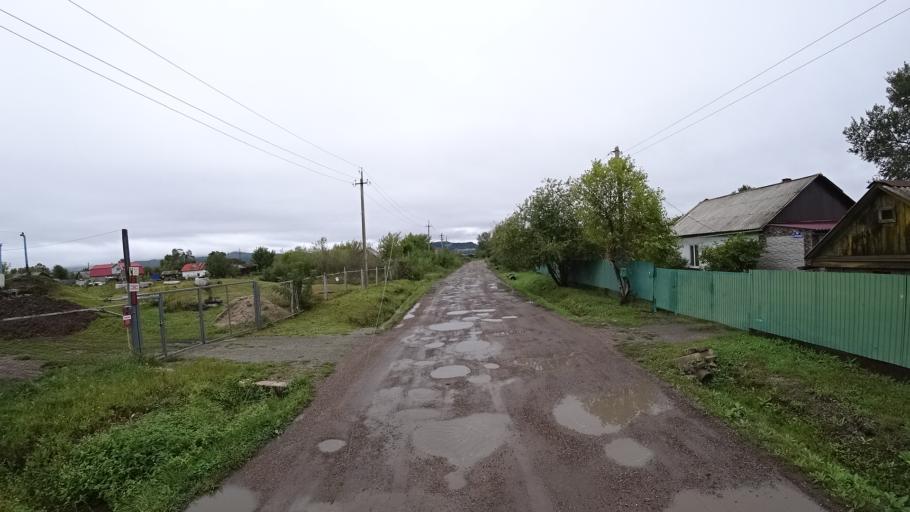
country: RU
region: Primorskiy
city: Monastyrishche
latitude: 44.1973
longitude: 132.4619
